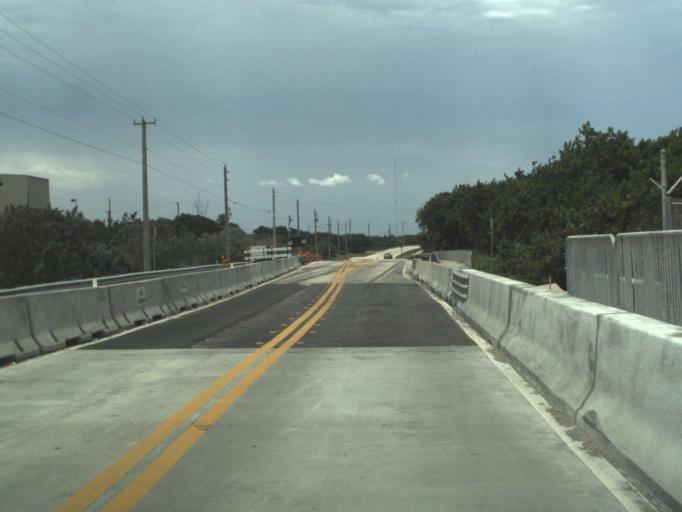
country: US
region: Florida
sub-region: Saint Lucie County
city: Hutchinson Island South
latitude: 27.3500
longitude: -80.2434
